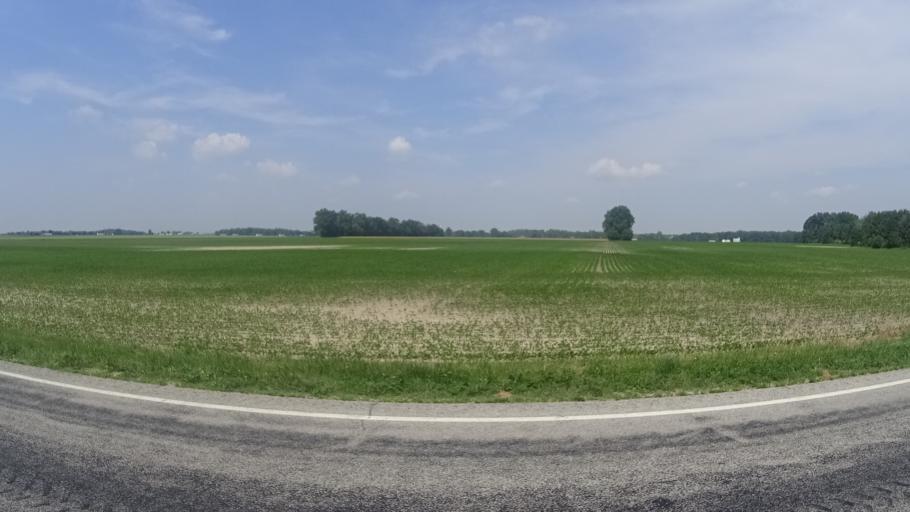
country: US
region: Ohio
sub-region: Huron County
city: Monroeville
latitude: 41.3444
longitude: -82.7244
